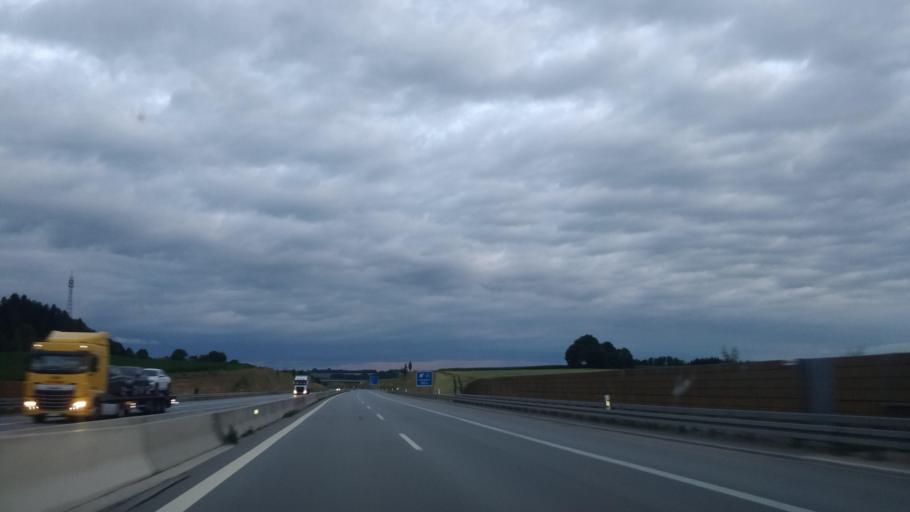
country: DE
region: Bavaria
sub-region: Upper Bavaria
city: Lengdorf
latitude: 48.2468
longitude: 12.0635
